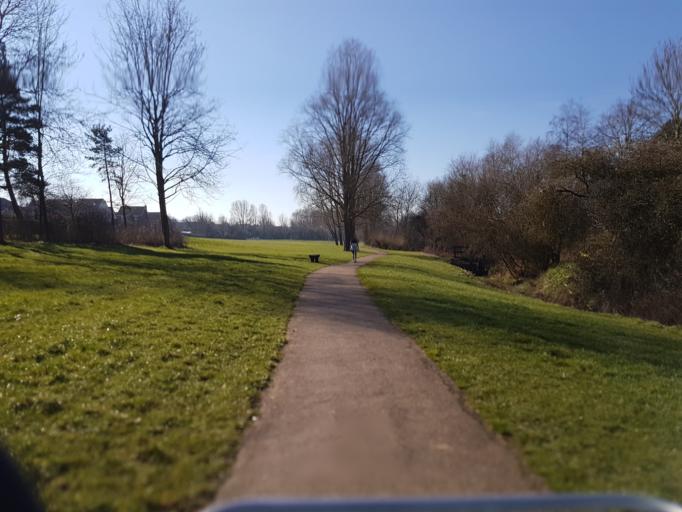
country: GB
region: England
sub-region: Milton Keynes
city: Shenley Church End
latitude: 52.0099
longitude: -0.7622
